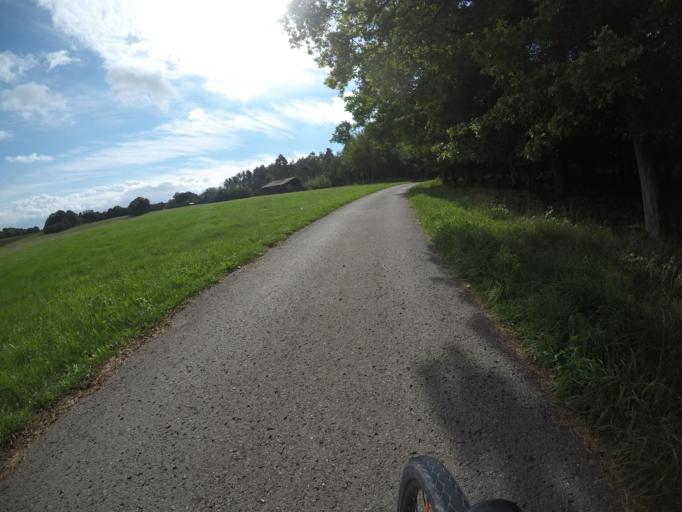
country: DE
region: Baden-Wuerttemberg
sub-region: Karlsruhe Region
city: Althengstett
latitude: 48.7174
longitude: 8.8049
